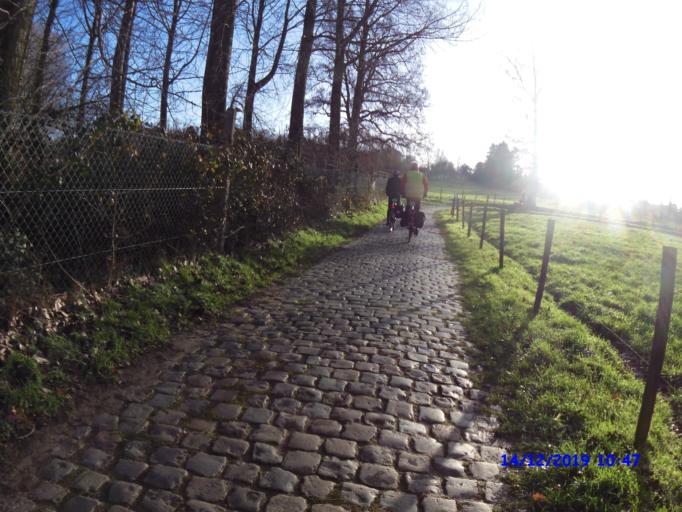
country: BE
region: Flanders
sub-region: Provincie Vlaams-Brabant
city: Beersel
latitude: 50.7728
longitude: 4.3032
